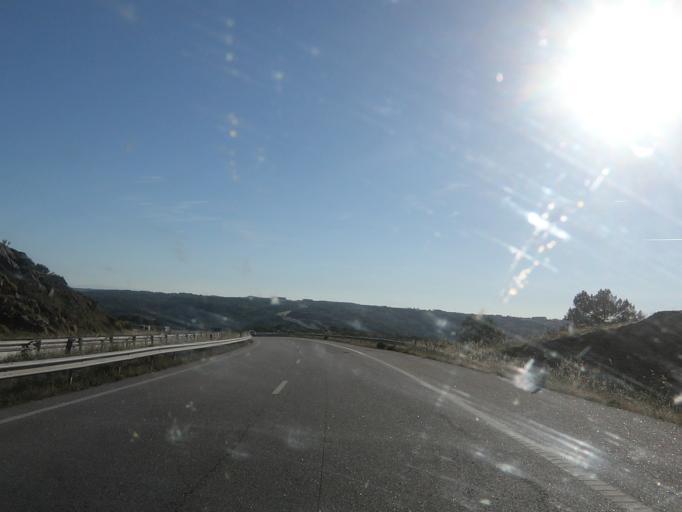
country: ES
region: Castille and Leon
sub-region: Provincia de Salamanca
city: Fuentes de Onoro
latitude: 40.6133
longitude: -6.8971
